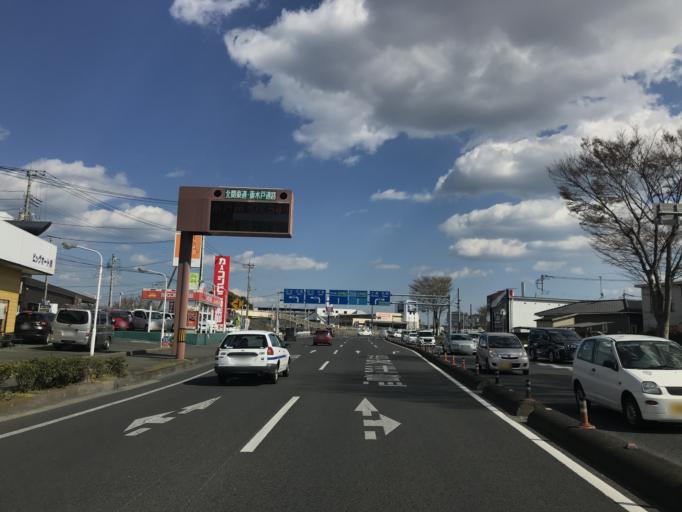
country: JP
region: Ibaraki
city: Mito-shi
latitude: 36.3416
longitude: 140.4802
